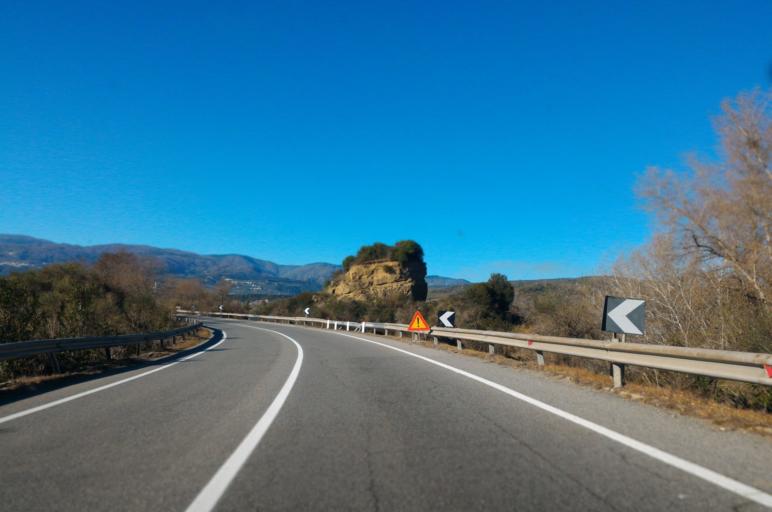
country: IT
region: Calabria
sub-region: Provincia di Crotone
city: Belvedere Spinello
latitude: 39.1914
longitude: 16.8813
